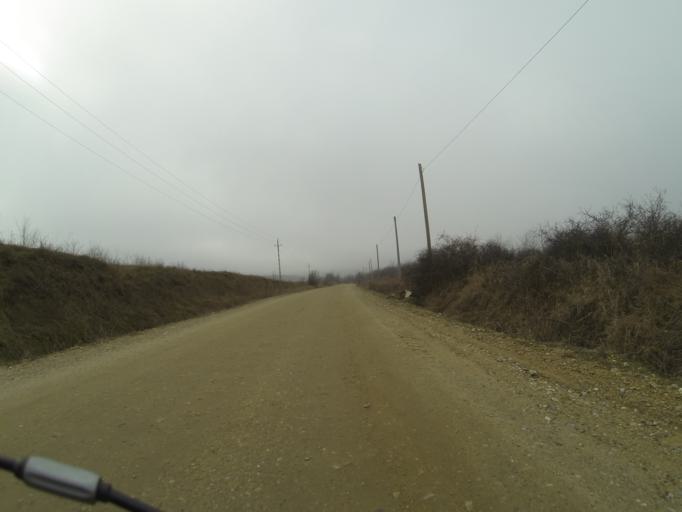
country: RO
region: Mehedinti
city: Dumbrava de Sus
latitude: 44.4886
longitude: 23.0797
